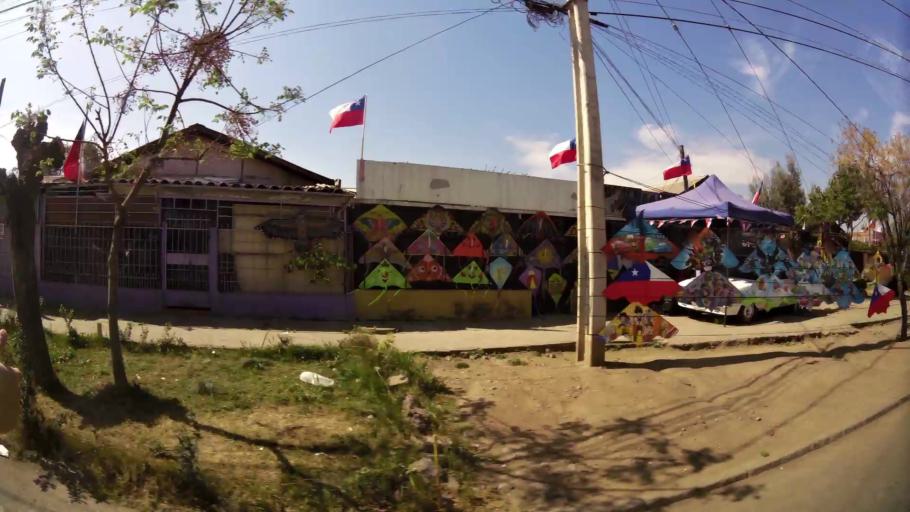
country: CL
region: Santiago Metropolitan
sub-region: Provincia de Santiago
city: Lo Prado
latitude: -33.4739
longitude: -70.7075
